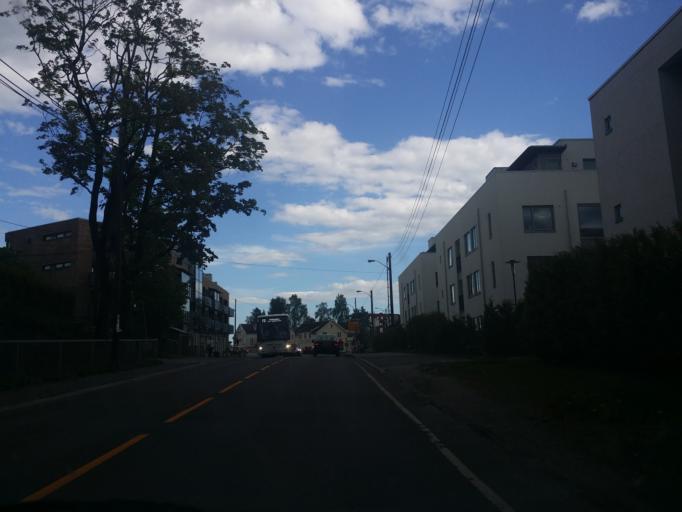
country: NO
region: Akershus
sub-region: Baerum
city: Lysaker
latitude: 59.9485
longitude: 10.6411
